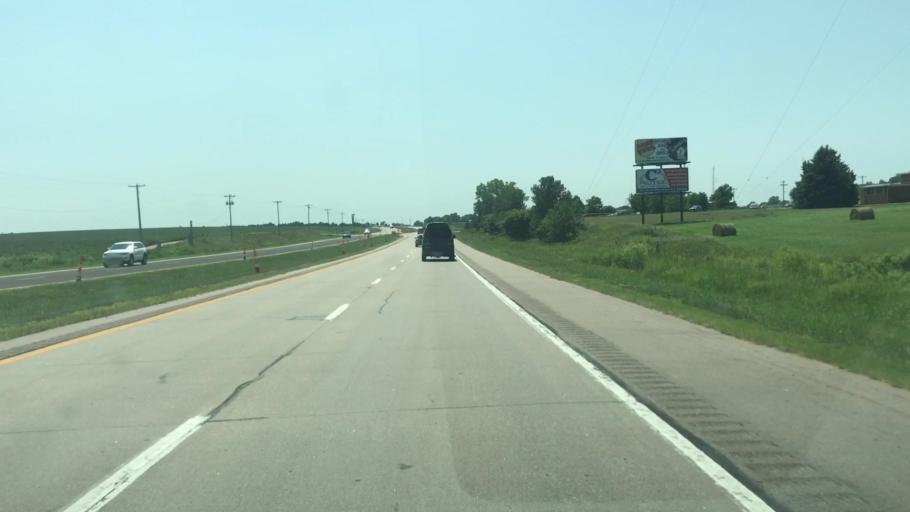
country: US
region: Nebraska
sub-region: Adams County
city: Hastings
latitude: 40.6501
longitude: -98.3826
